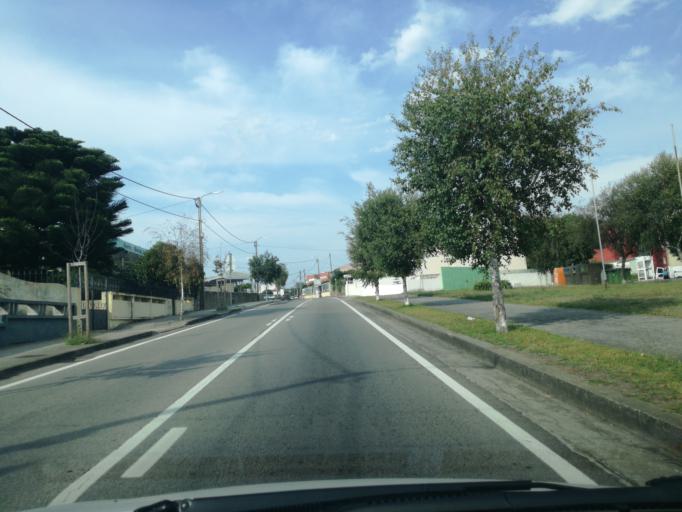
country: PT
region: Aveiro
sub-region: Espinho
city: Espinho
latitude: 41.0159
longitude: -8.6330
